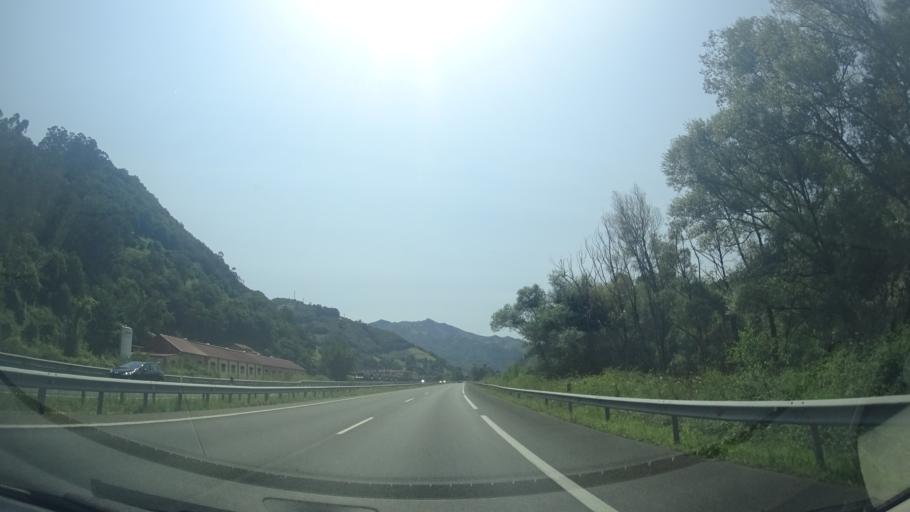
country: ES
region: Asturias
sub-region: Province of Asturias
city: Mieres
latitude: 43.2180
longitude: -5.7838
